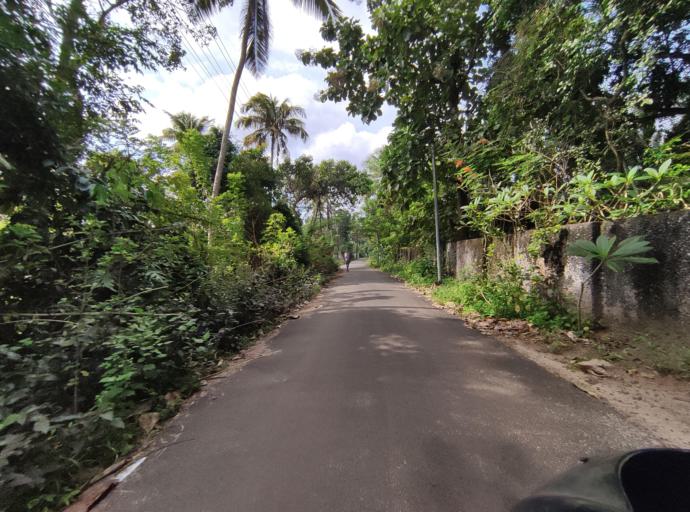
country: IN
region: Kerala
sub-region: Alappuzha
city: Vayalar
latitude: 9.6927
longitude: 76.3309
